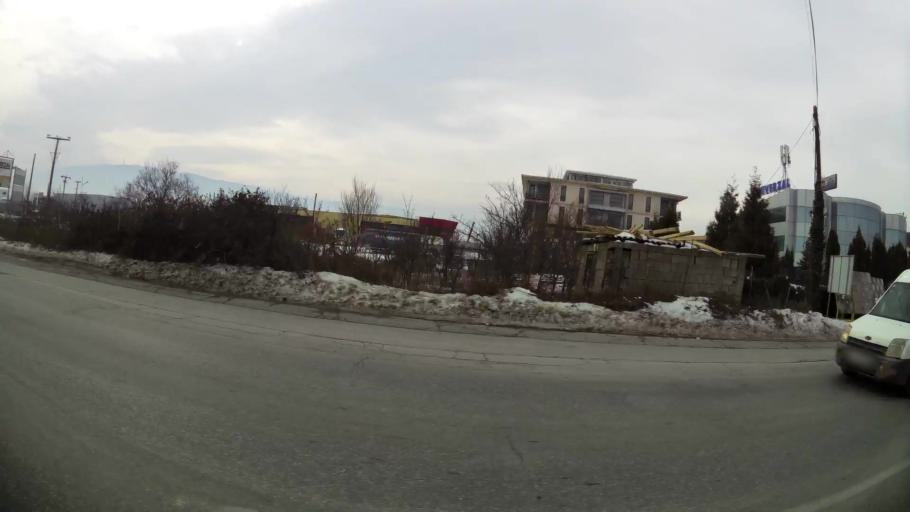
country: MK
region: Suto Orizari
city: Suto Orizare
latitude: 42.0342
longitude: 21.4012
